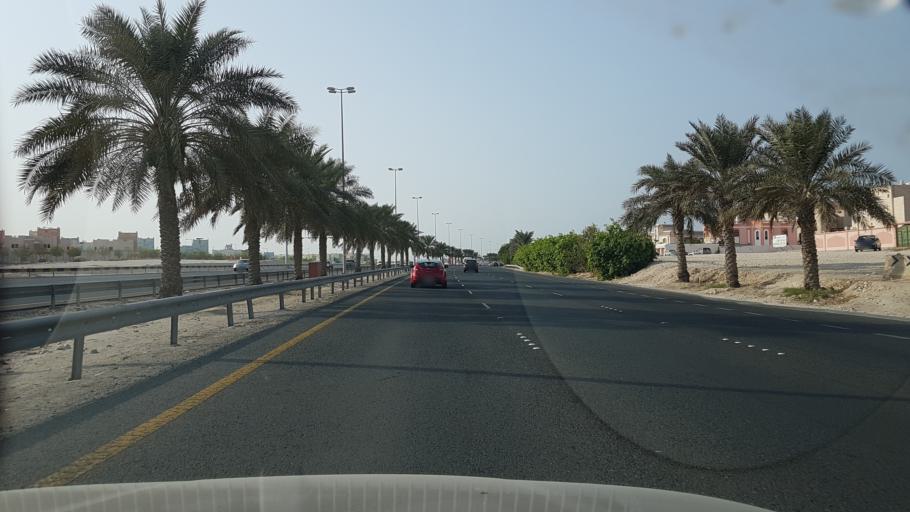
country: BH
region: Central Governorate
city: Madinat Hamad
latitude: 26.1347
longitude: 50.5097
